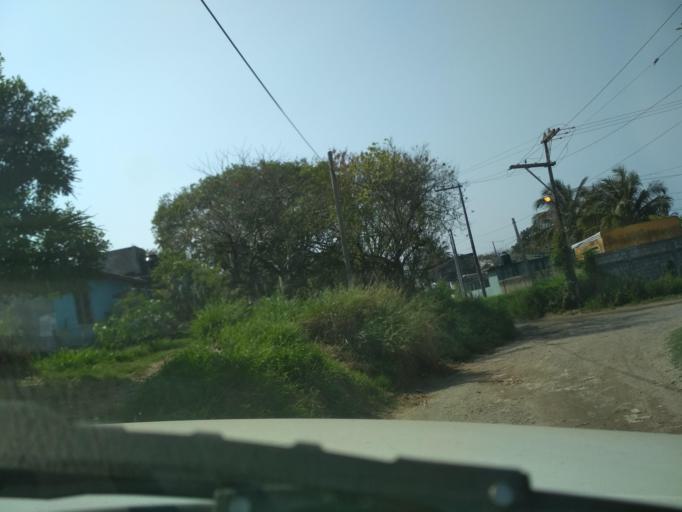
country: MX
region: Veracruz
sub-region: Veracruz
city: Colonia Chalchihuecan
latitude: 19.2128
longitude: -96.2130
